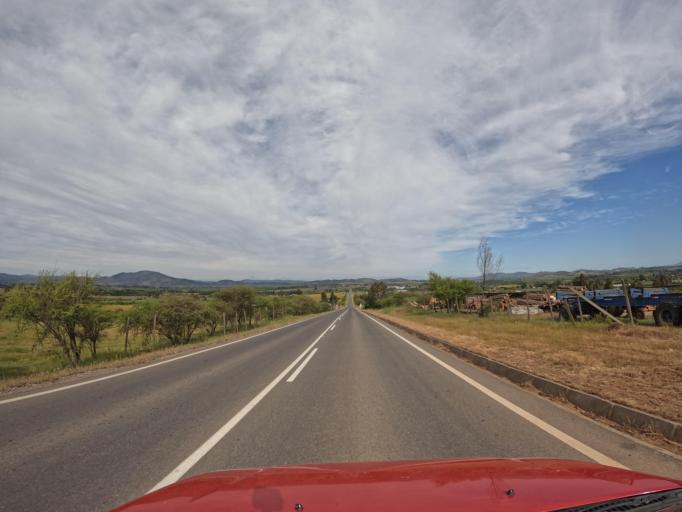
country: CL
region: Maule
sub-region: Provincia de Talca
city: Talca
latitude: -35.3699
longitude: -71.8460
